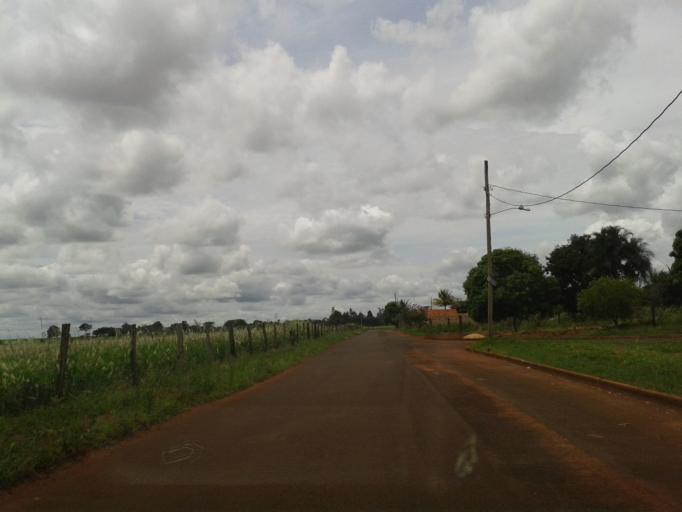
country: BR
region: Minas Gerais
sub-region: Centralina
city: Centralina
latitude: -18.5790
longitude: -49.2081
